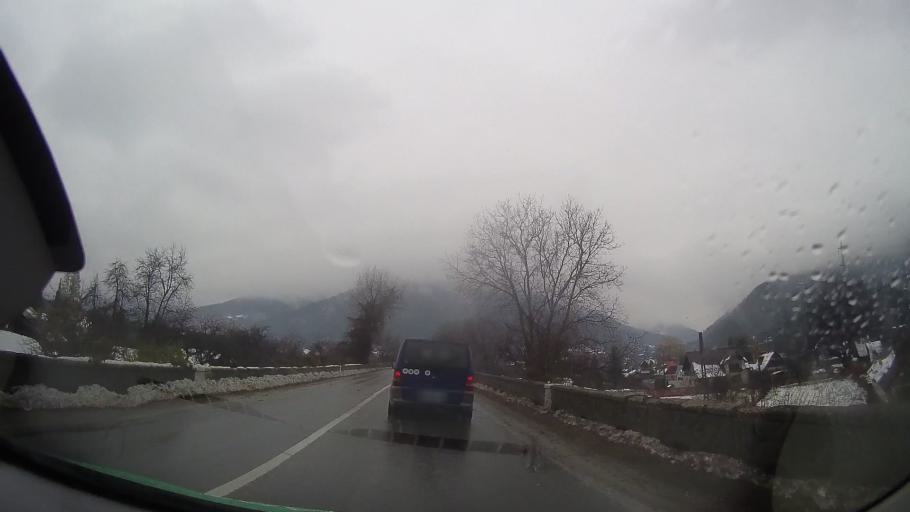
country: RO
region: Neamt
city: Viisoara
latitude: 46.9290
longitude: 26.2247
